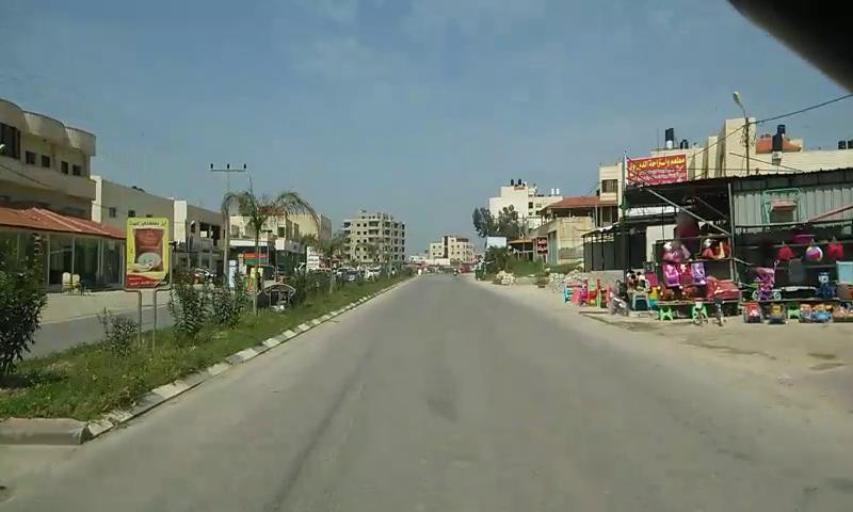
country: PS
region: West Bank
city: Janin
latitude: 32.4837
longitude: 35.2995
